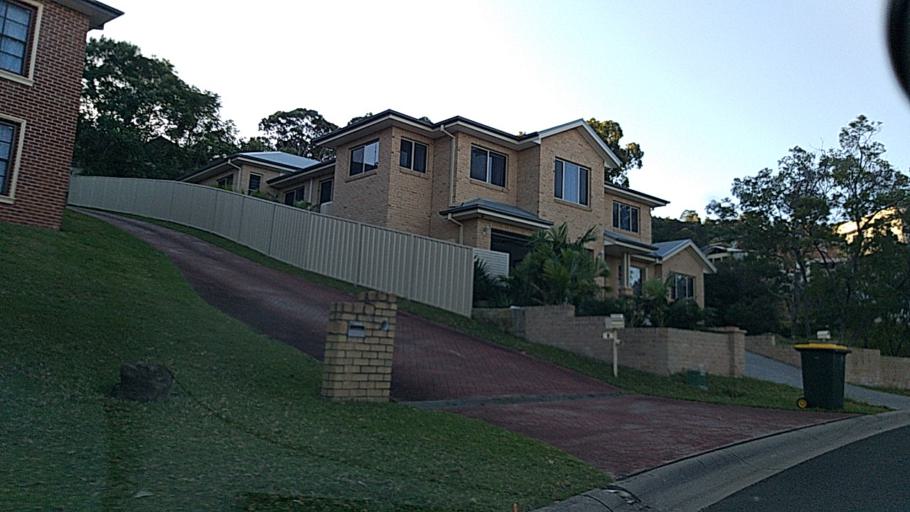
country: AU
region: New South Wales
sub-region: Wollongong
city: Mount Keira
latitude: -34.4226
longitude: 150.8458
